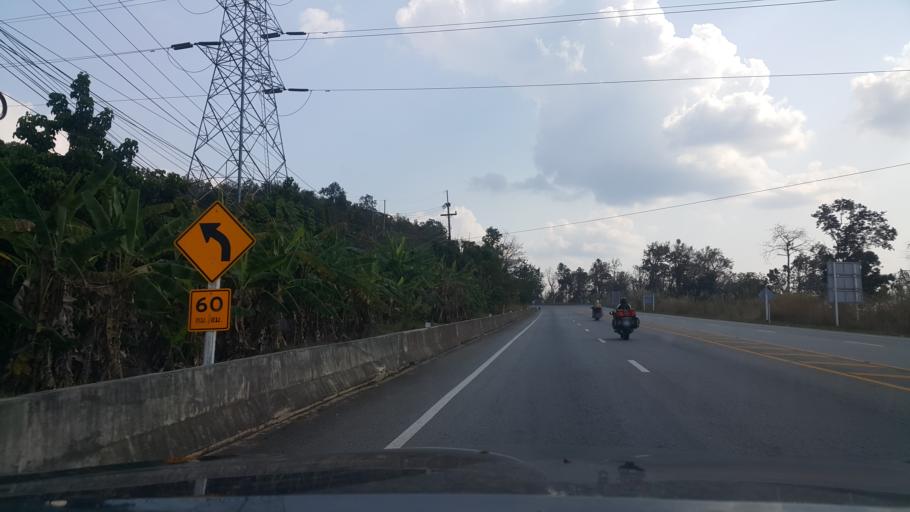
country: TH
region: Phitsanulok
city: Nakhon Thai
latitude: 16.8839
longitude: 100.8124
